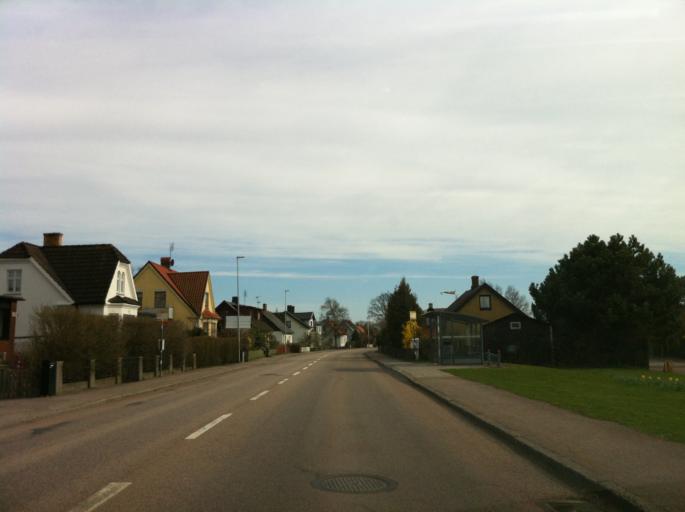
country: SE
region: Skane
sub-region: Hoganas Kommun
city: Hoganas
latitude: 56.2114
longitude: 12.5535
